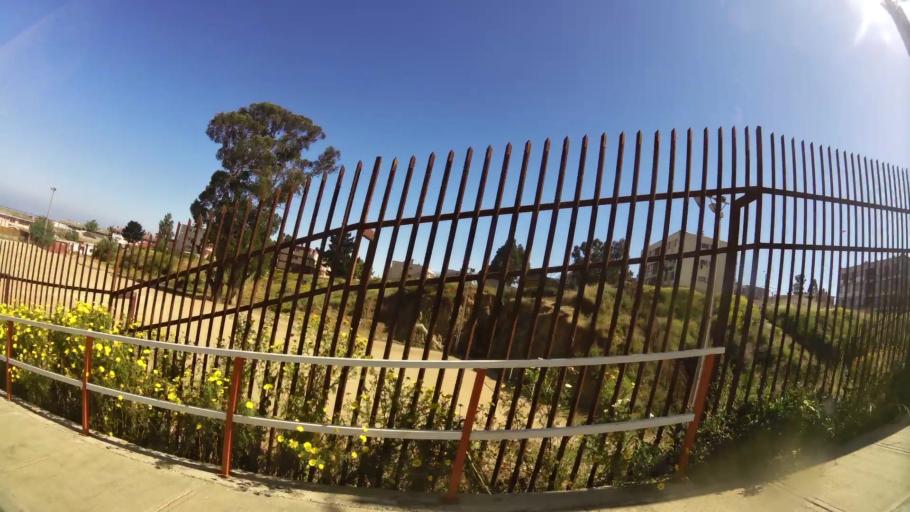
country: CL
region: Valparaiso
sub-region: Provincia de Valparaiso
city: Valparaiso
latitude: -33.0522
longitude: -71.6505
